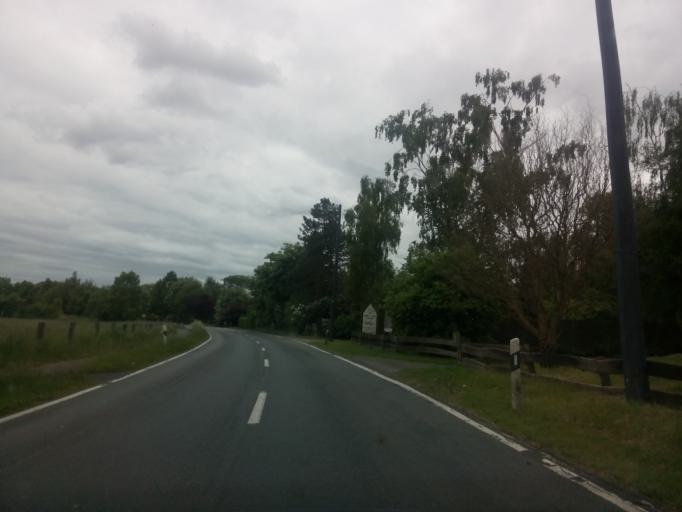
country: DE
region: Lower Saxony
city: Delmenhorst
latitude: 53.0920
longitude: 8.6685
